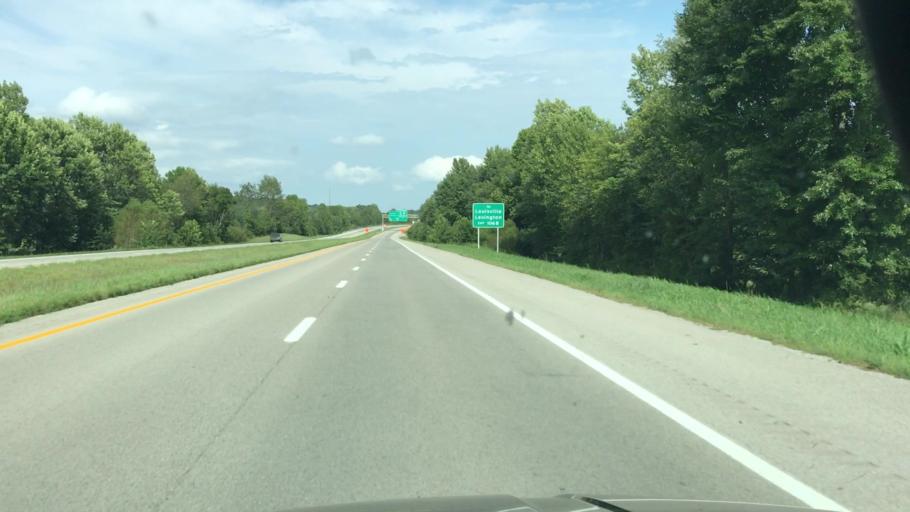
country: US
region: Kentucky
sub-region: Hopkins County
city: Nortonville
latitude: 37.2114
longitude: -87.4767
